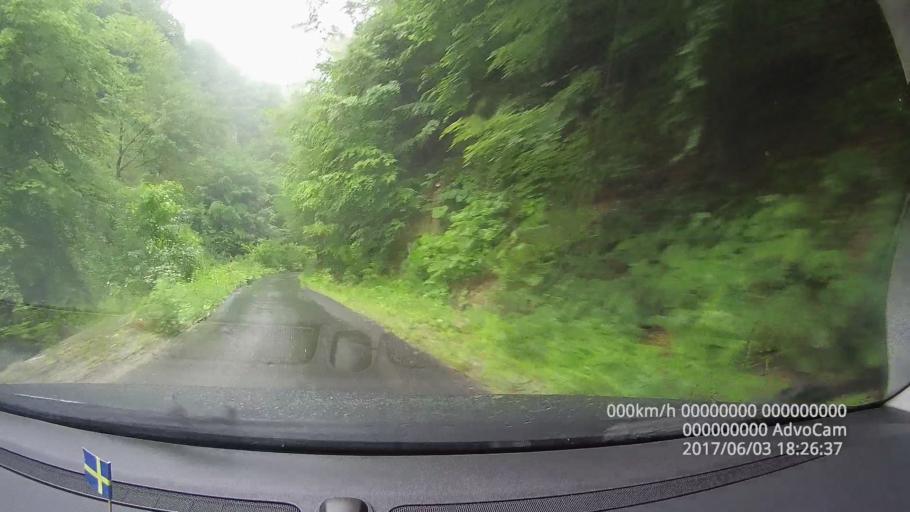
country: RO
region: Gorj
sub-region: Comuna Runcu
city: Dobrita
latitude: 45.1680
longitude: 23.1911
